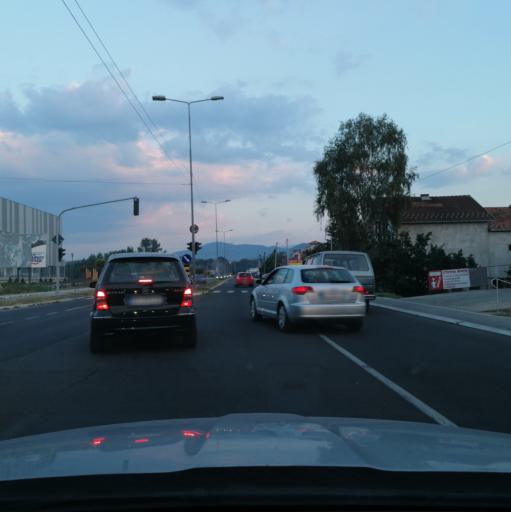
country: RS
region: Central Serbia
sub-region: Raski Okrug
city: Kraljevo
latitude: 43.7155
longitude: 20.6926
